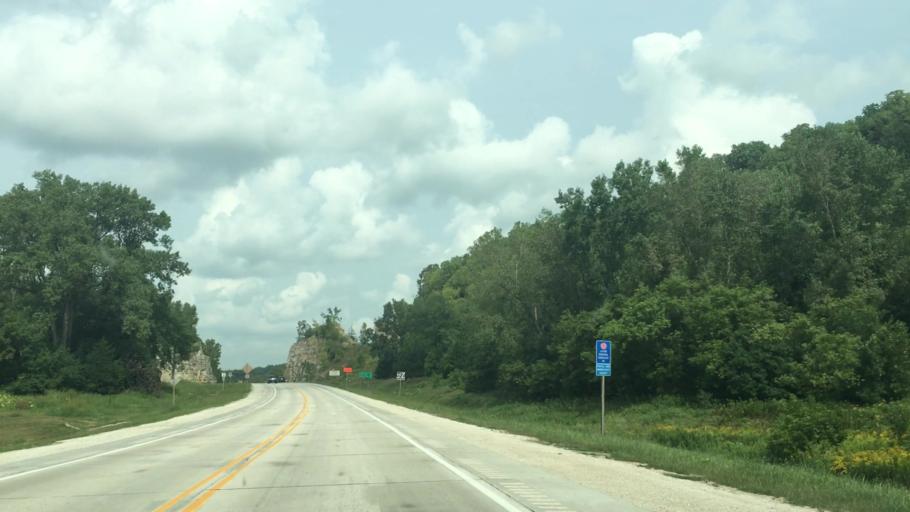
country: US
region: Iowa
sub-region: Winneshiek County
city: Decorah
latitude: 43.2929
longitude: -91.8061
